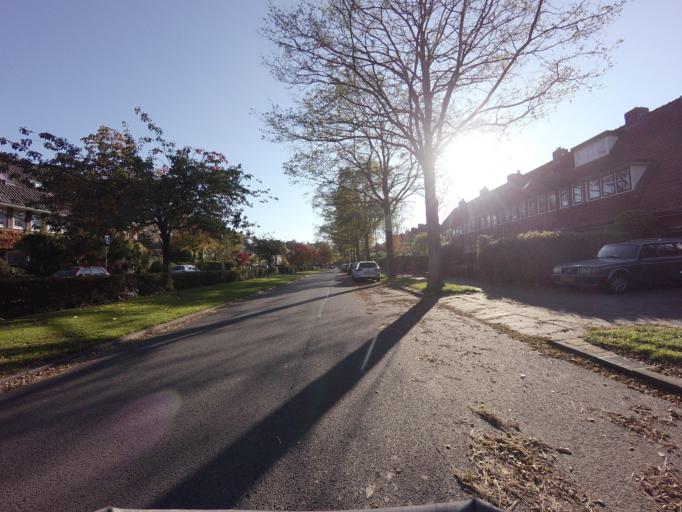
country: NL
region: North Holland
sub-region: Gemeente Hilversum
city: Hilversum
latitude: 52.2099
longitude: 5.1670
